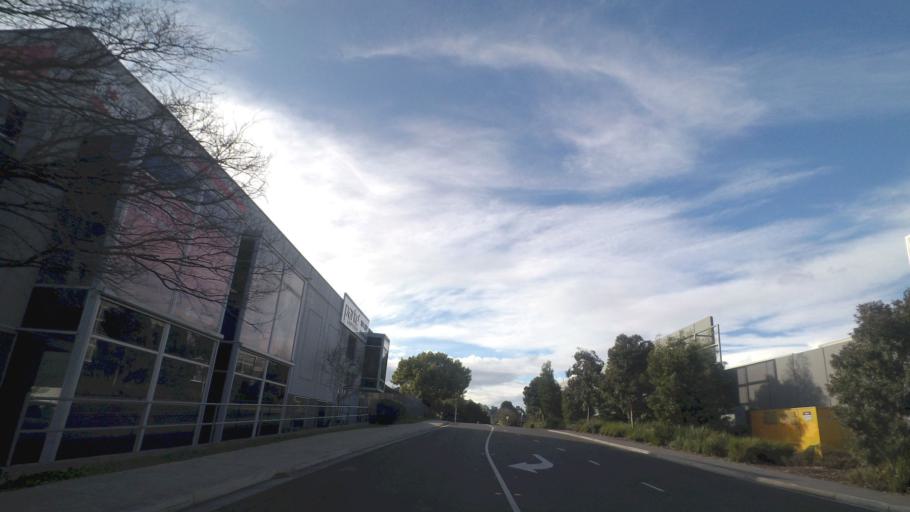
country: AU
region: Victoria
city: Mitcham
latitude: -37.8150
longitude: 145.2240
